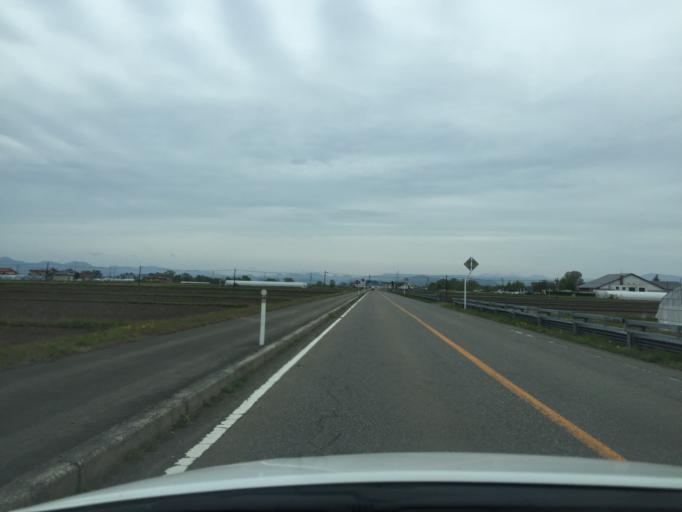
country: JP
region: Fukushima
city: Inawashiro
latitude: 37.5412
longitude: 140.0778
